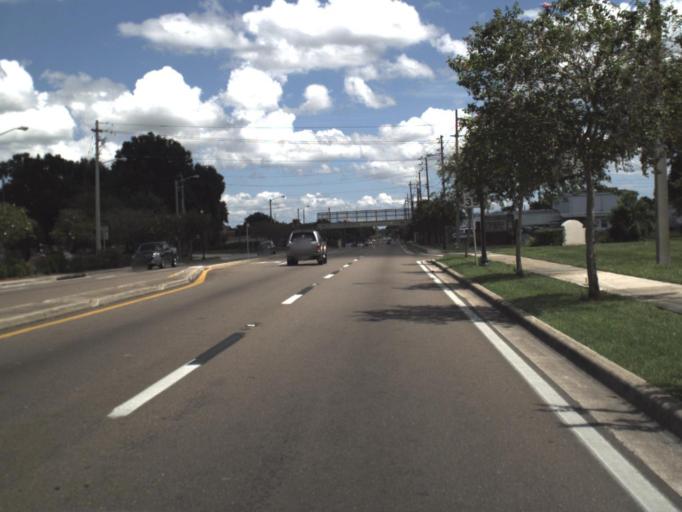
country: US
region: Florida
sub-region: Polk County
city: Winter Haven
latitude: 28.0440
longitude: -81.7337
